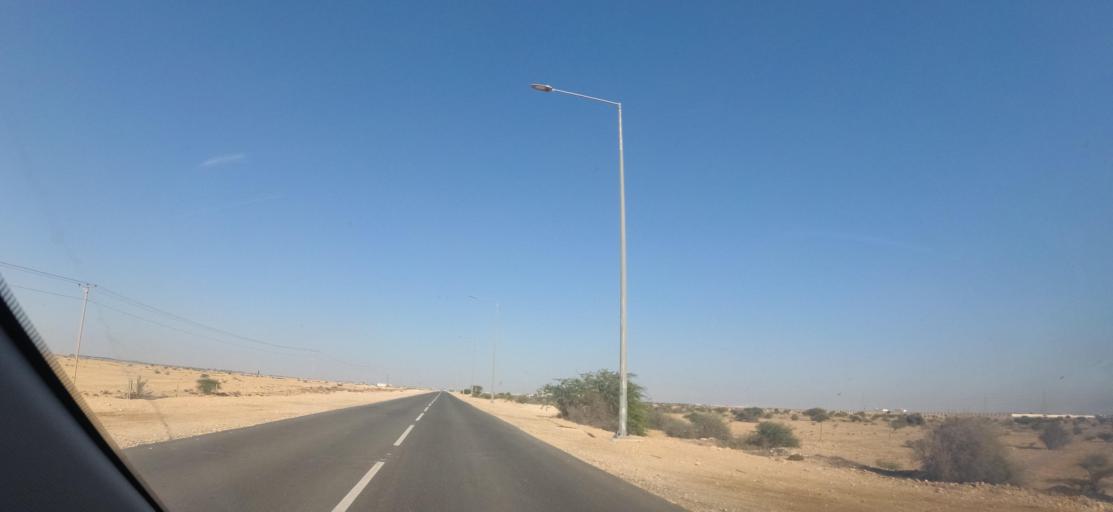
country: QA
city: Al Ghuwayriyah
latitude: 25.8406
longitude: 51.2609
